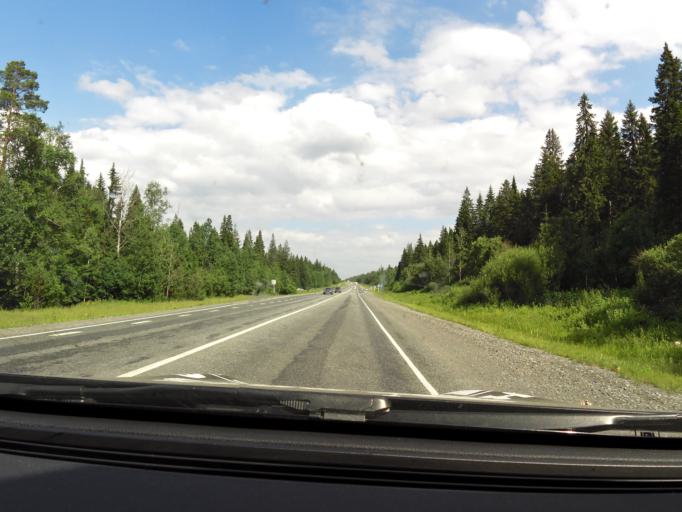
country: RU
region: Sverdlovsk
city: Bisert'
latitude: 56.8263
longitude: 59.2215
